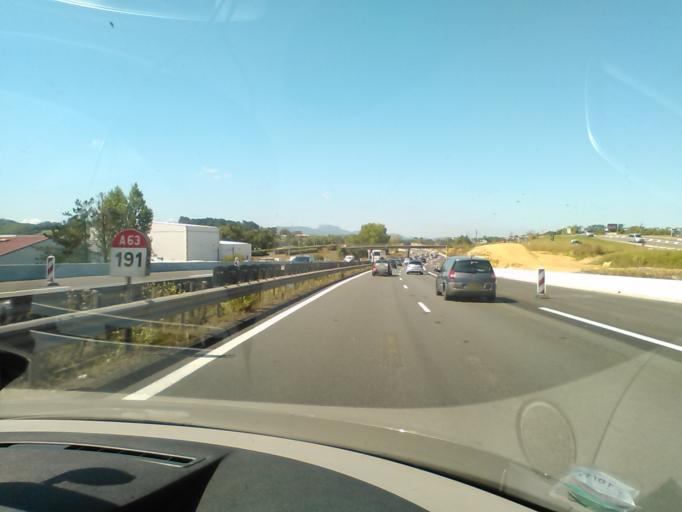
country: FR
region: Aquitaine
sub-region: Departement des Pyrenees-Atlantiques
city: Guethary
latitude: 43.4083
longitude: -1.6238
